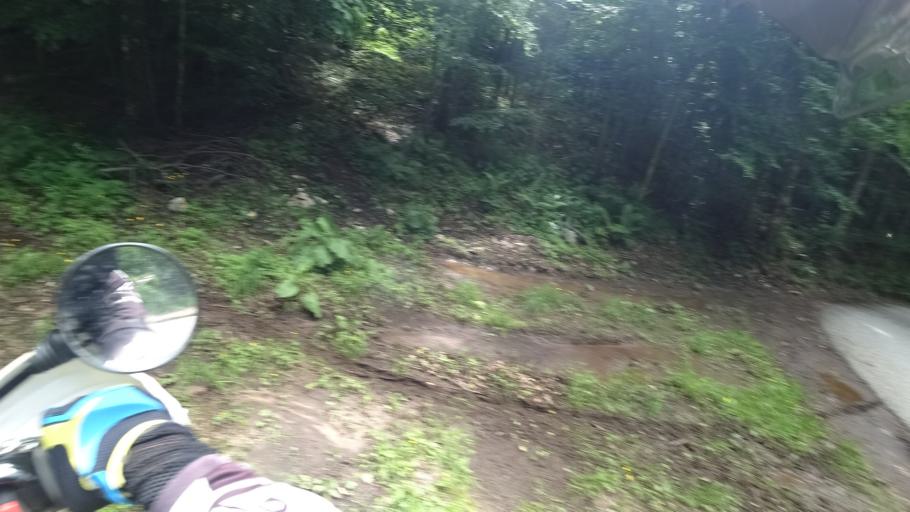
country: HR
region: Primorsko-Goranska
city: Bribir
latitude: 45.2514
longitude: 14.7898
